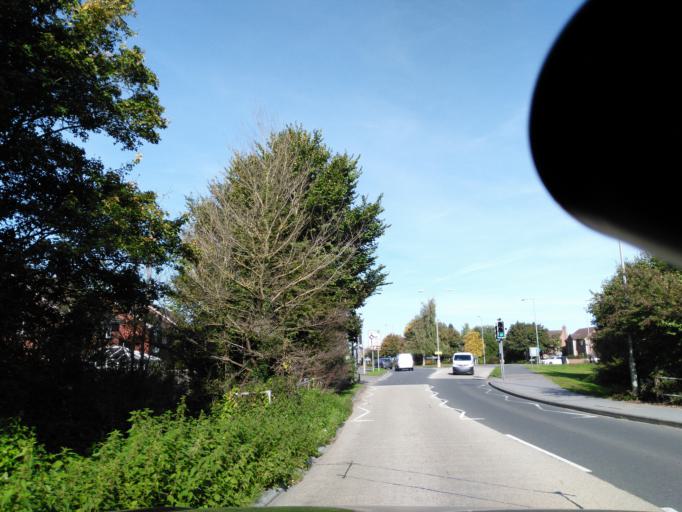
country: GB
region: England
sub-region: Wiltshire
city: Melksham
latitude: 51.3658
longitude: -2.1274
